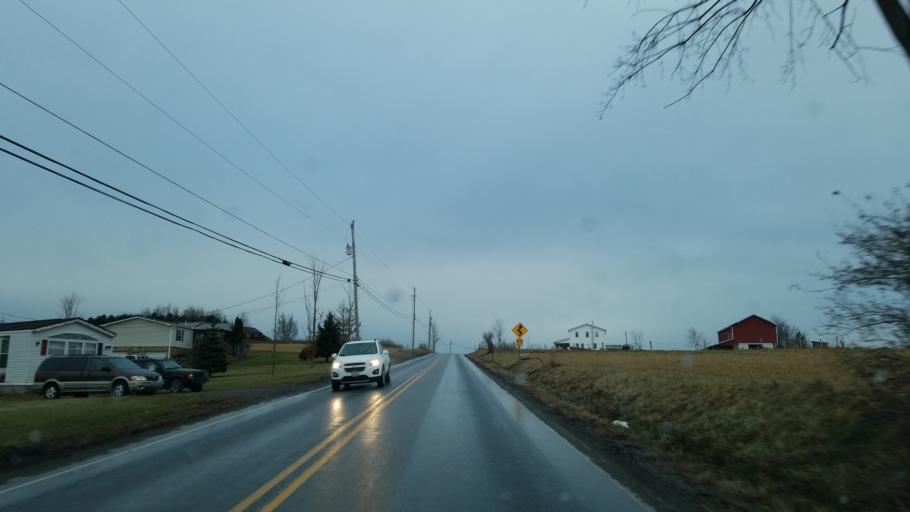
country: US
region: Pennsylvania
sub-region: Jefferson County
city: Sykesville
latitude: 41.0357
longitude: -78.7539
